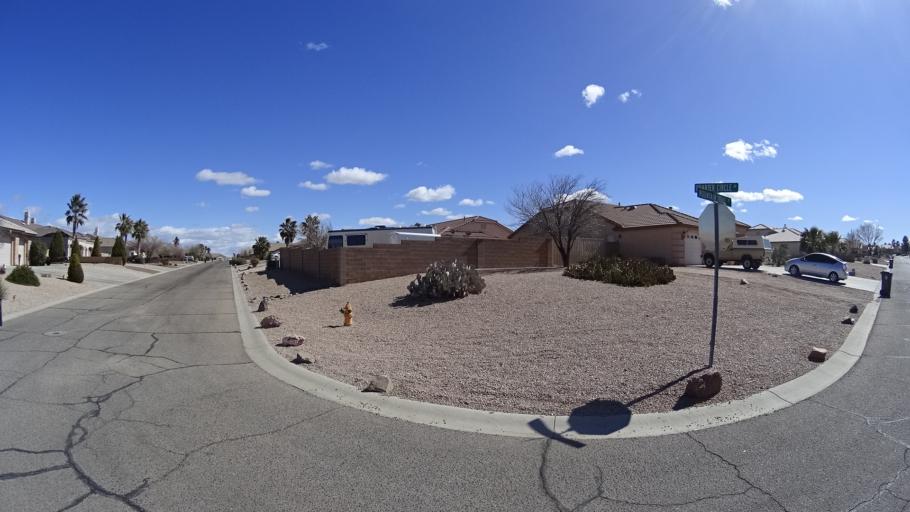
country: US
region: Arizona
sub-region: Mohave County
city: New Kingman-Butler
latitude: 35.2098
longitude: -113.9753
